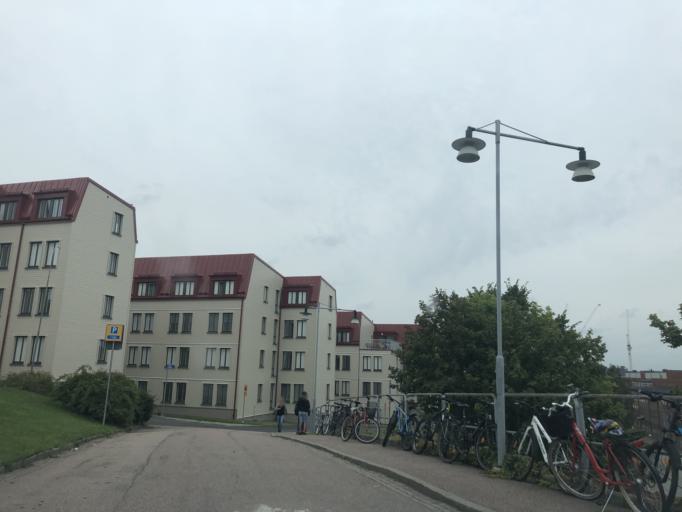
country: SE
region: Vaestra Goetaland
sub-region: Goteborg
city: Majorna
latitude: 57.7044
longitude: 11.9328
